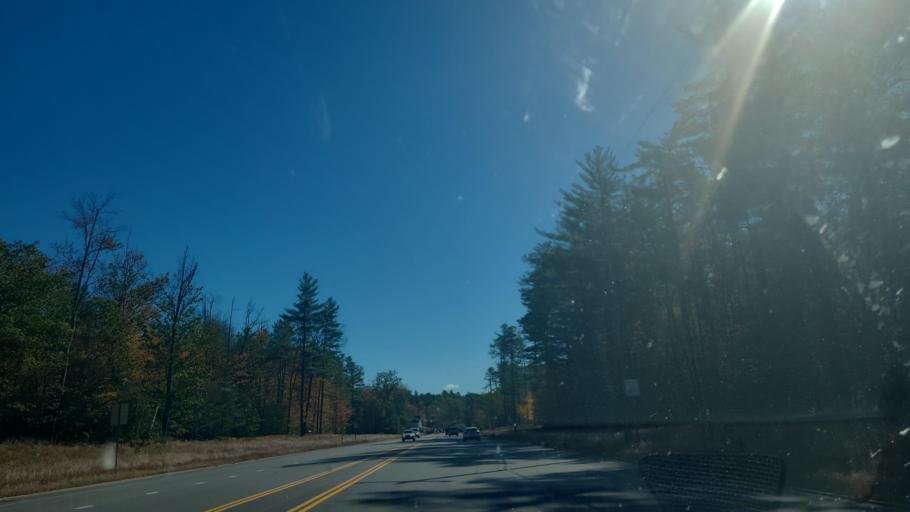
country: US
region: New Hampshire
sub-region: Carroll County
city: Conway
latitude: 44.0155
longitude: -71.1058
